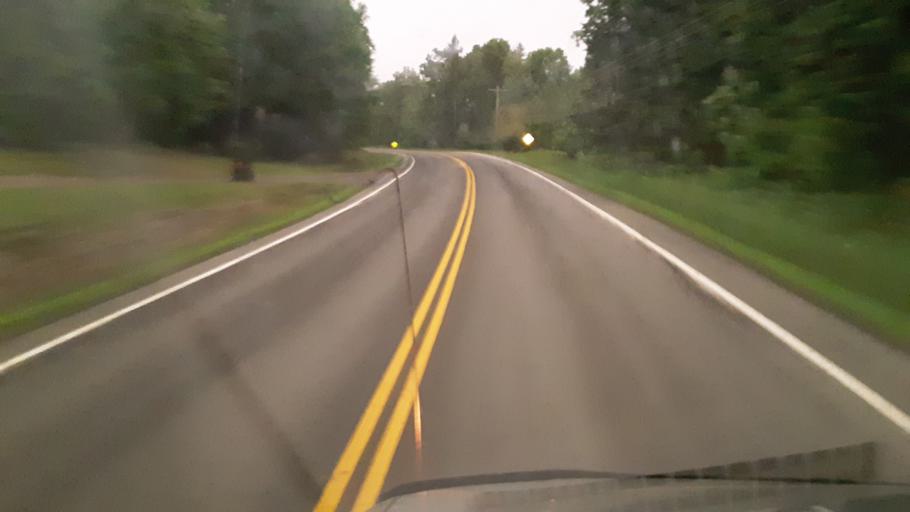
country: US
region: Maine
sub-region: Penobscot County
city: Patten
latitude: 46.0703
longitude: -68.4378
